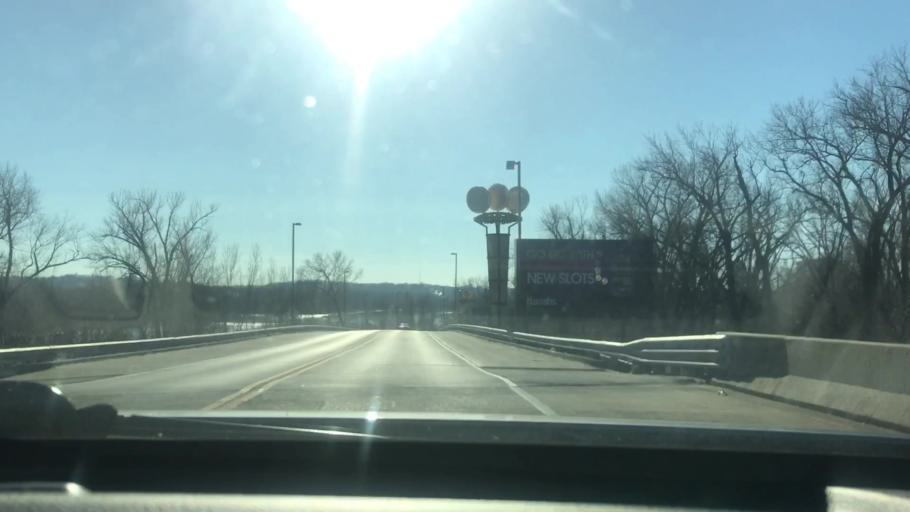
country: US
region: Missouri
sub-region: Clay County
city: North Kansas City
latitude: 39.1466
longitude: -94.5390
